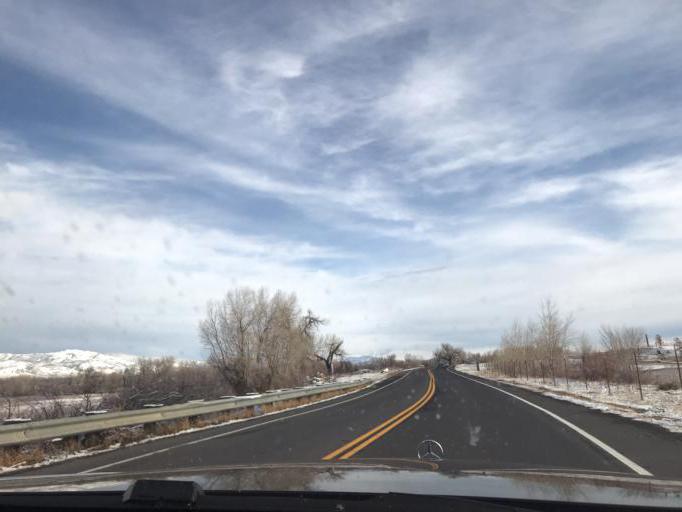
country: US
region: Colorado
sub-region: Boulder County
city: Superior
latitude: 39.9937
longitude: -105.2124
